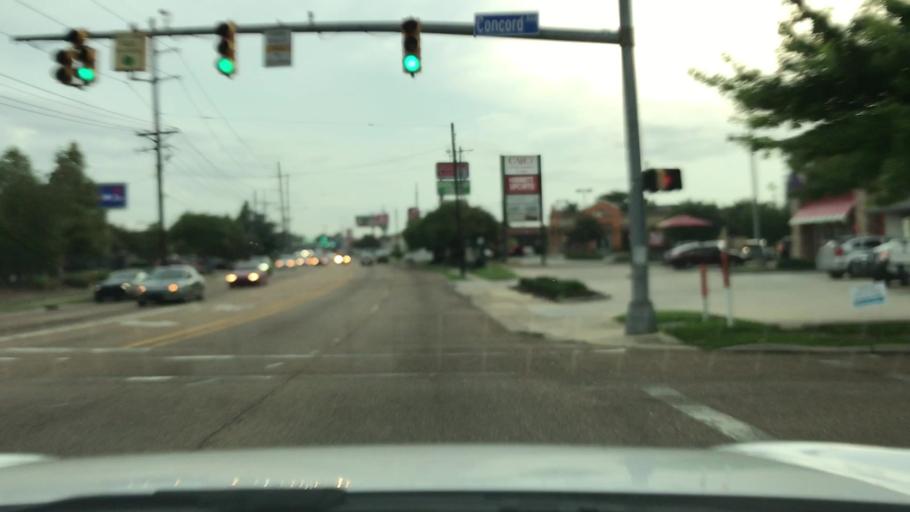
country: US
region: Louisiana
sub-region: East Baton Rouge Parish
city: Baton Rouge
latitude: 30.4184
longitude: -91.1418
